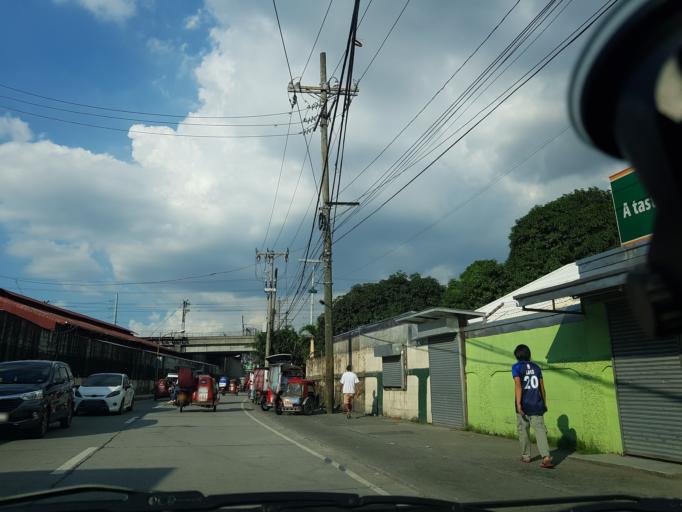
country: PH
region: Metro Manila
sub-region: Marikina
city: Calumpang
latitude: 14.6228
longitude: 121.0838
